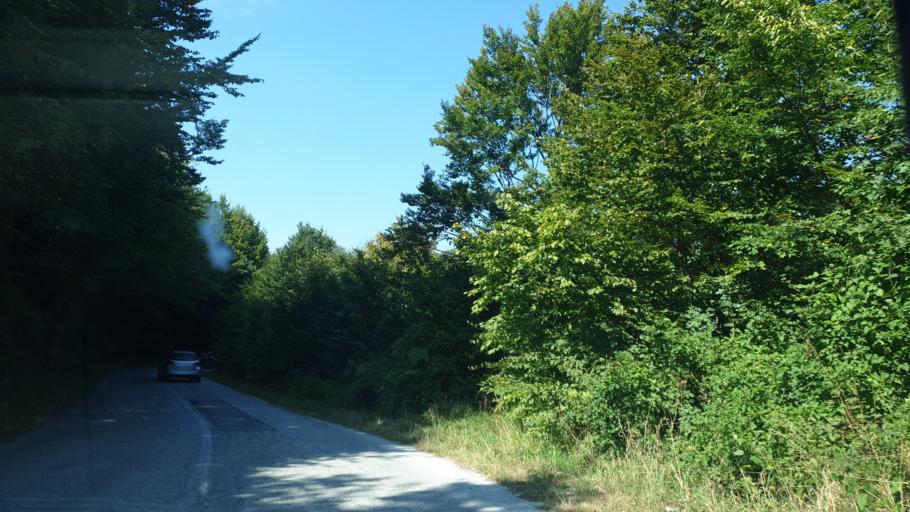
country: RS
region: Central Serbia
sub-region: Zlatiborski Okrug
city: Cajetina
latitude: 43.7076
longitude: 19.8410
